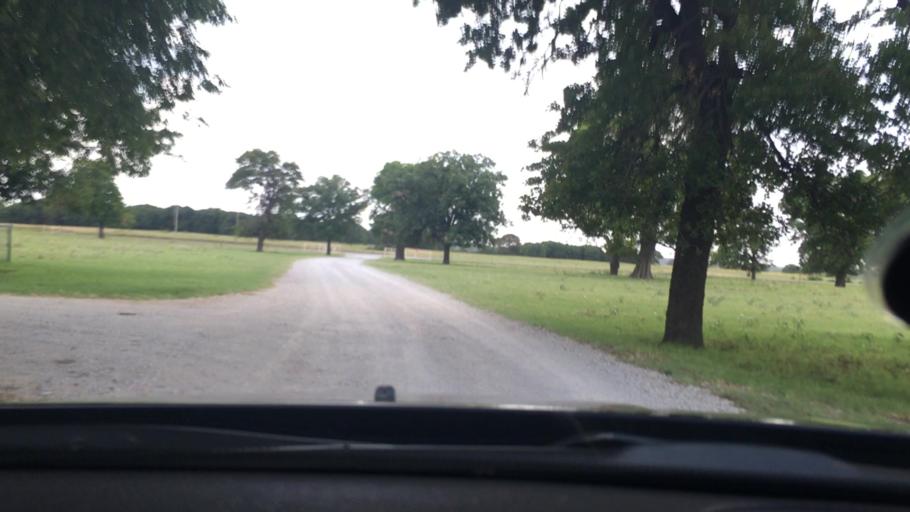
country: US
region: Oklahoma
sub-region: Carter County
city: Wilson
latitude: 33.9419
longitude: -97.4167
